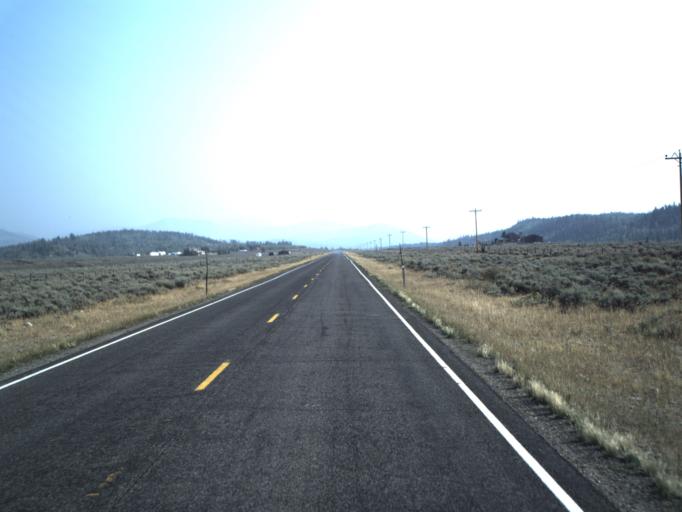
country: US
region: Wyoming
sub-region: Uinta County
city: Evanston
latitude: 40.9502
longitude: -110.8409
